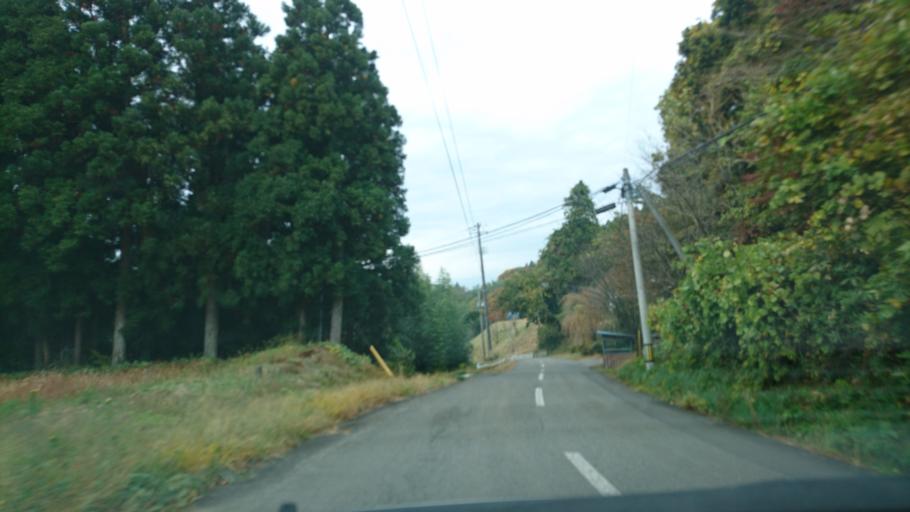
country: JP
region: Iwate
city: Ichinoseki
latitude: 38.9764
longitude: 141.1648
